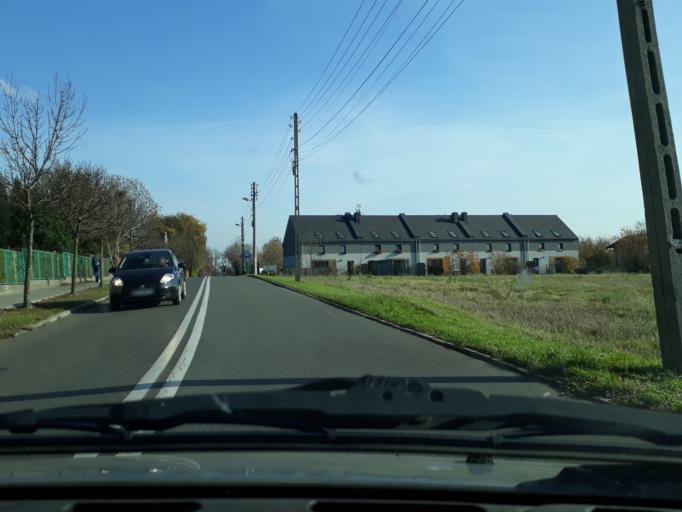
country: PL
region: Silesian Voivodeship
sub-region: Powiat tarnogorski
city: Tarnowskie Gory
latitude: 50.4253
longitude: 18.8491
